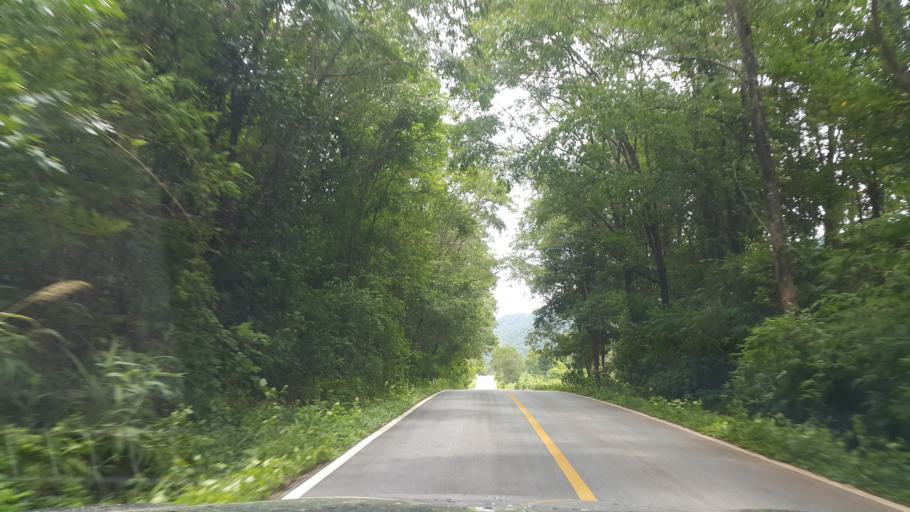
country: TH
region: Phitsanulok
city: Chat Trakan
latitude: 17.3521
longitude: 100.7255
